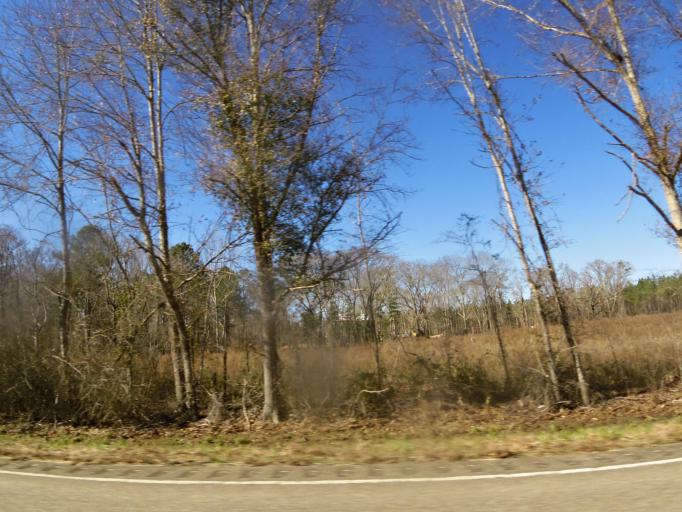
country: US
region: Alabama
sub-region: Bullock County
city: Union Springs
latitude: 32.1170
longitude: -85.7827
